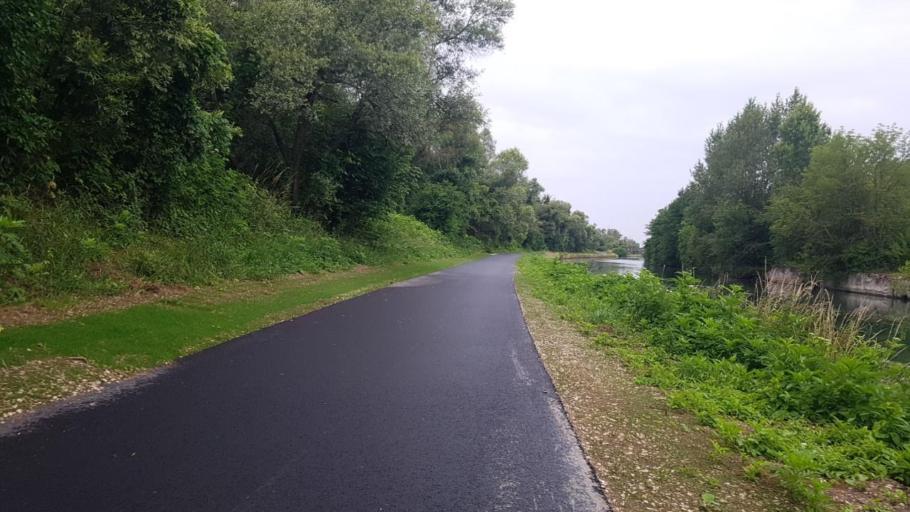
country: FR
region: Champagne-Ardenne
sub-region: Departement de la Marne
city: Vitry-le-Francois
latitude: 48.7768
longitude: 4.5424
